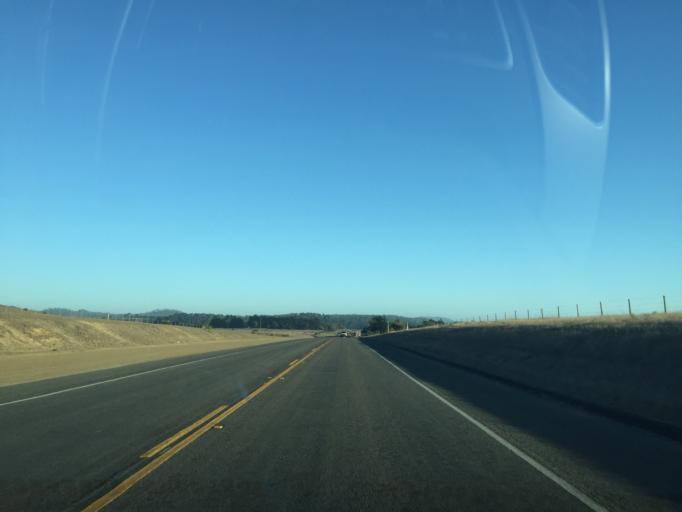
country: US
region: California
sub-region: San Luis Obispo County
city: Cambria
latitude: 35.6052
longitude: -121.1351
